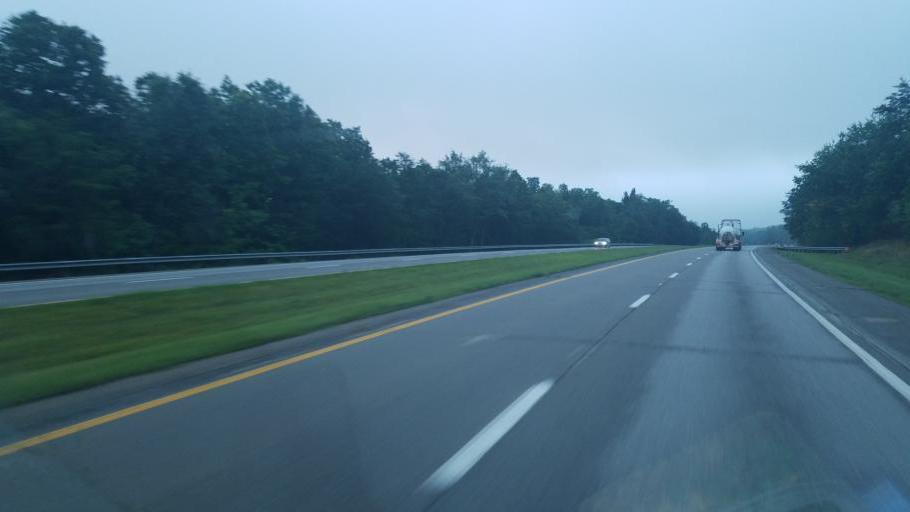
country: US
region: Ohio
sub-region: Jackson County
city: Jackson
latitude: 39.0203
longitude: -82.5786
